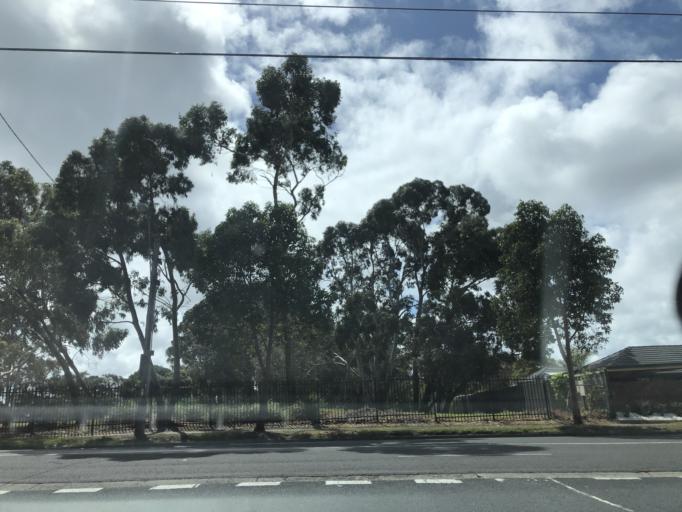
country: AU
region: Victoria
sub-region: Monash
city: Oakleigh South
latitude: -37.9253
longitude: 145.0914
